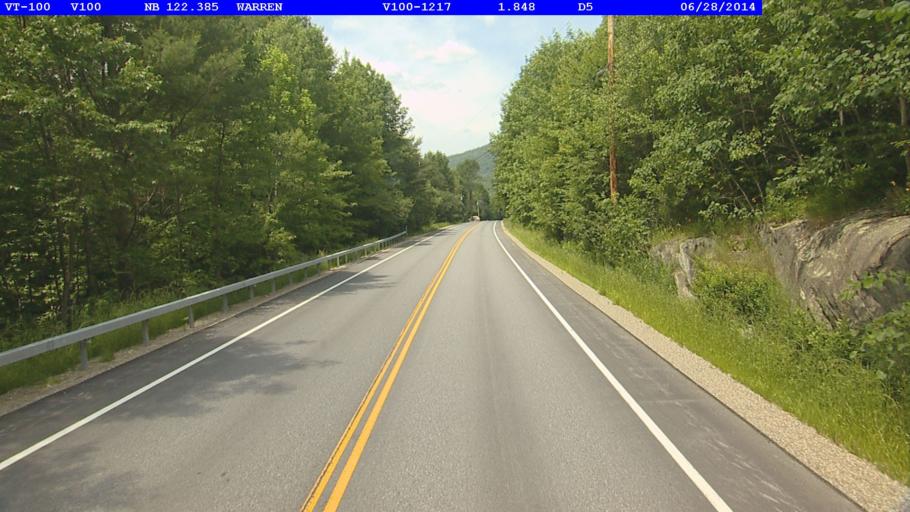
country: US
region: Vermont
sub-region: Washington County
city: Northfield
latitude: 44.0857
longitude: -72.8612
